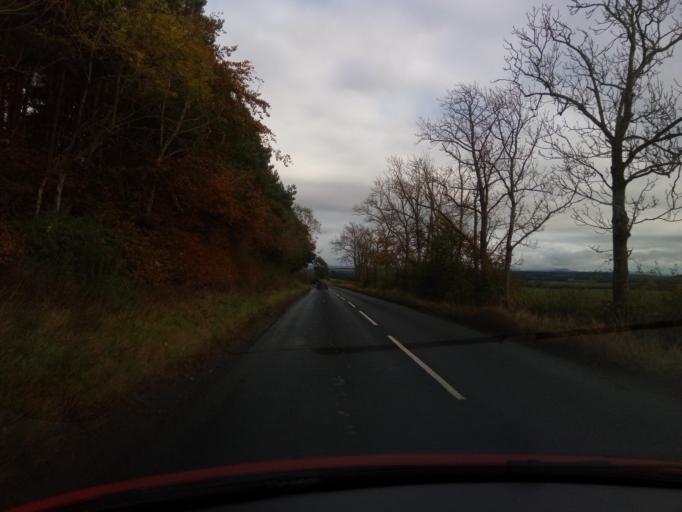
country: GB
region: Scotland
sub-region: The Scottish Borders
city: Newtown St Boswells
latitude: 55.5621
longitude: -2.6938
